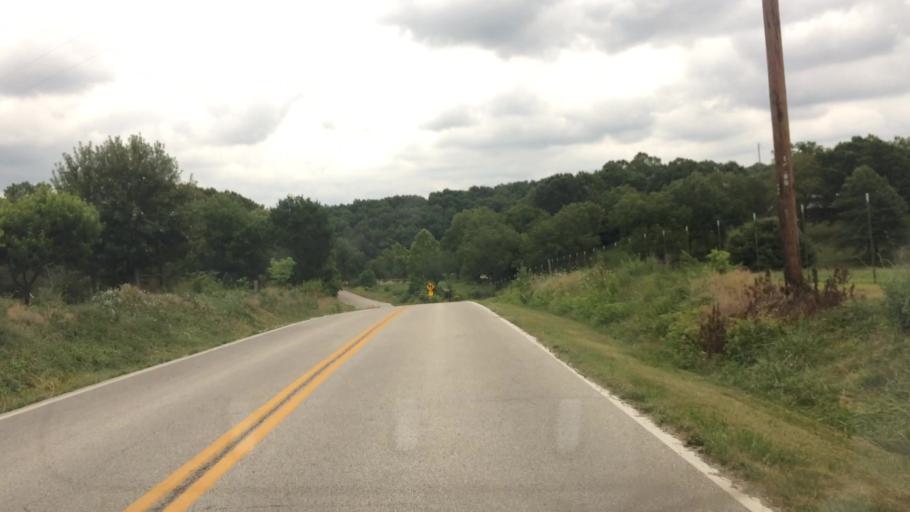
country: US
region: Missouri
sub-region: Greene County
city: Strafford
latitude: 37.2887
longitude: -93.0906
